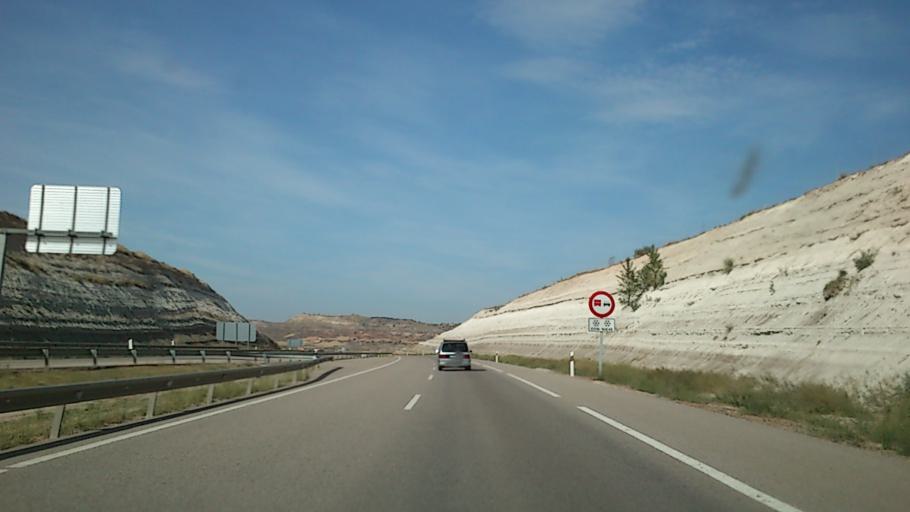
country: ES
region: Aragon
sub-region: Provincia de Teruel
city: Calamocha
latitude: 40.9187
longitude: -1.2699
